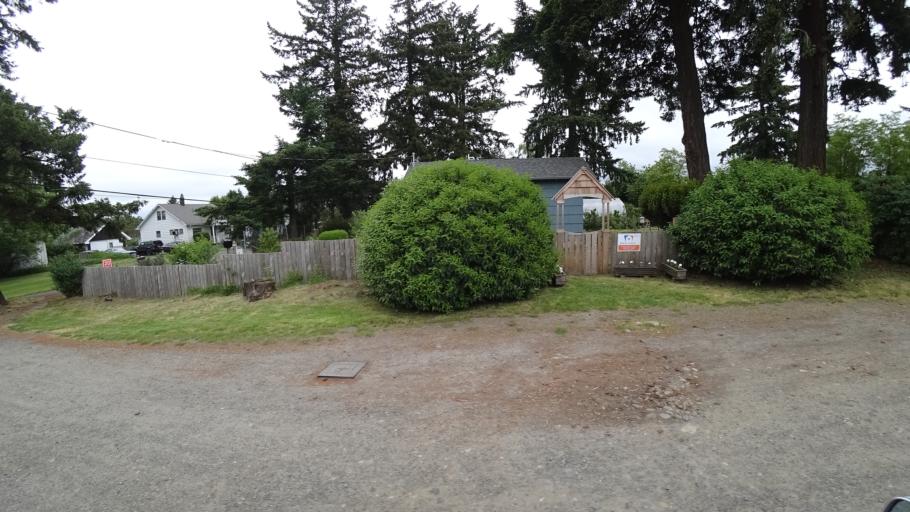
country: US
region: Oregon
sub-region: Multnomah County
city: Portland
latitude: 45.5522
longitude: -122.6123
